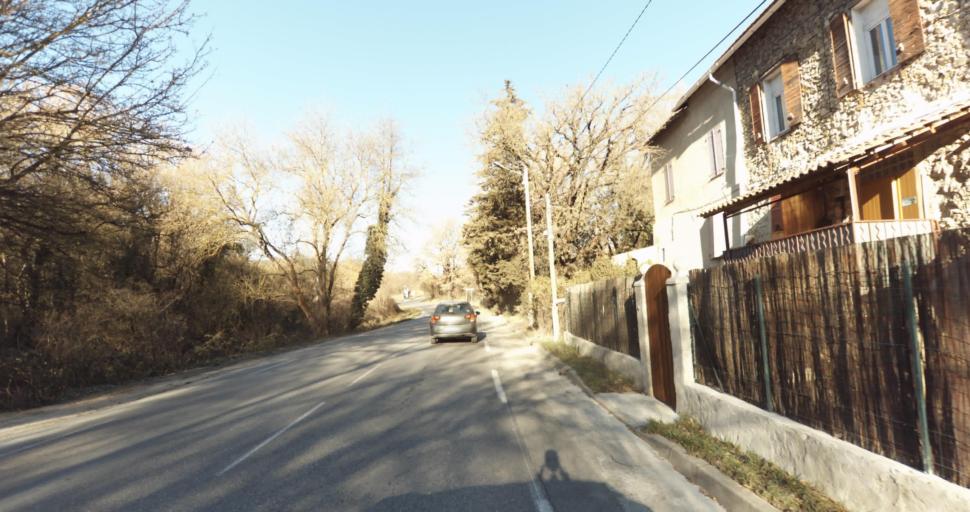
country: FR
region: Provence-Alpes-Cote d'Azur
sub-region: Departement des Bouches-du-Rhone
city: Peypin
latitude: 43.3969
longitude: 5.5727
